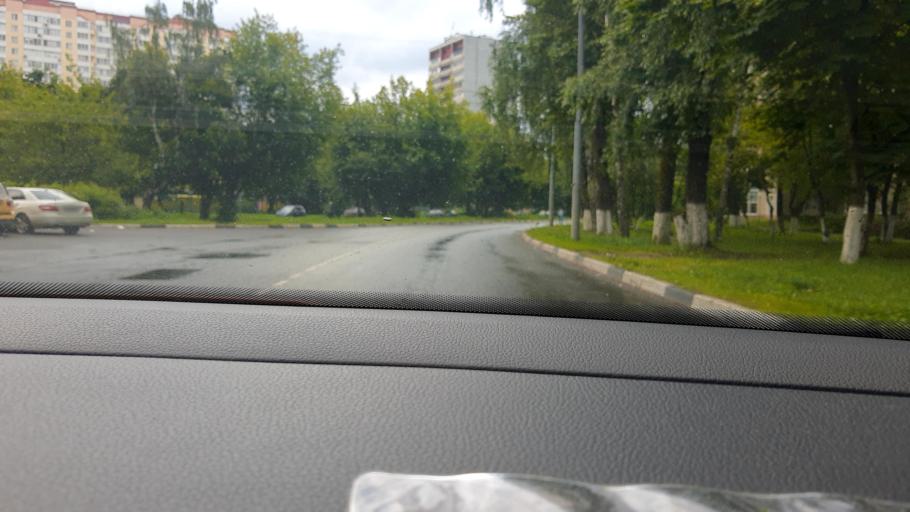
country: RU
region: Moskovskaya
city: Zheleznodorozhnyy
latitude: 55.7486
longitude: 37.9996
